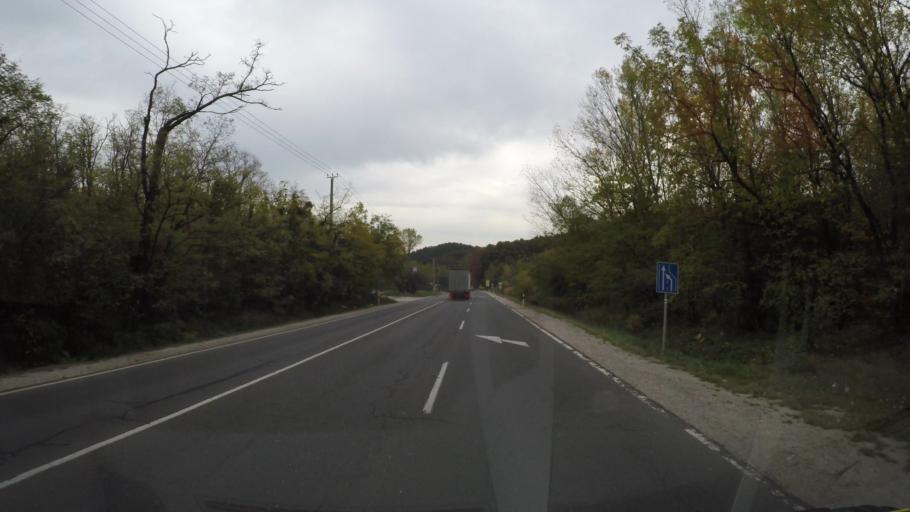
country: HU
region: Pest
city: Piliscsaba
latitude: 47.6235
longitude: 18.8629
